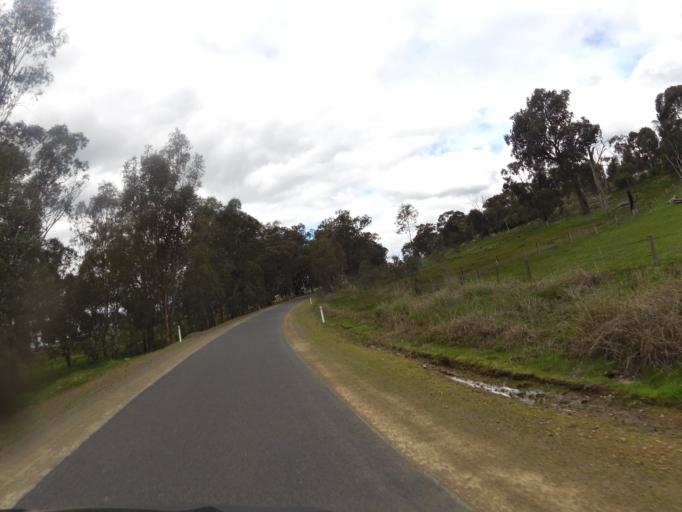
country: AU
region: Victoria
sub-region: Benalla
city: Benalla
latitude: -36.6725
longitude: 145.9389
